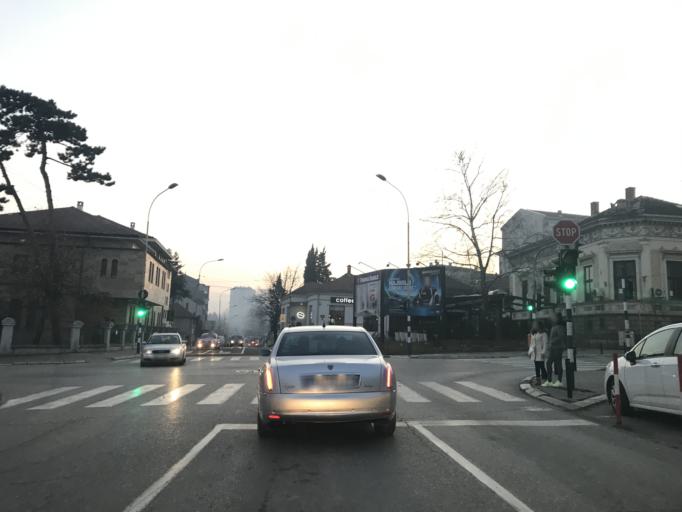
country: RS
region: Central Serbia
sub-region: Sumadijski Okrug
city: Kragujevac
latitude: 44.0129
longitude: 20.9121
